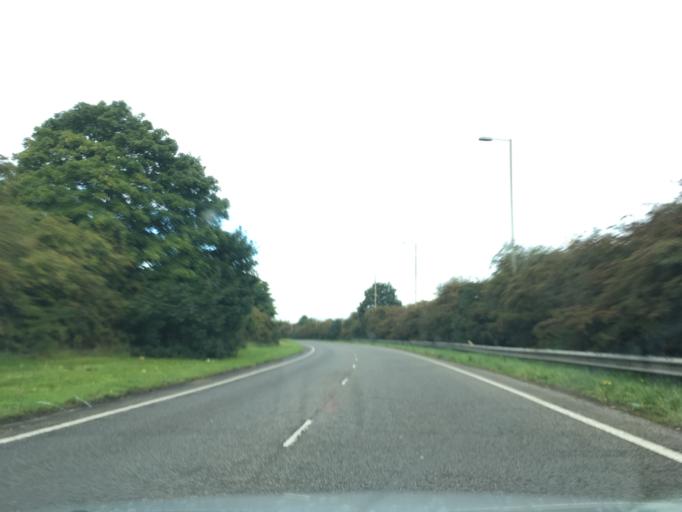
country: GB
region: England
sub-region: Oxfordshire
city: Cowley
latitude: 51.7645
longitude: -1.1986
